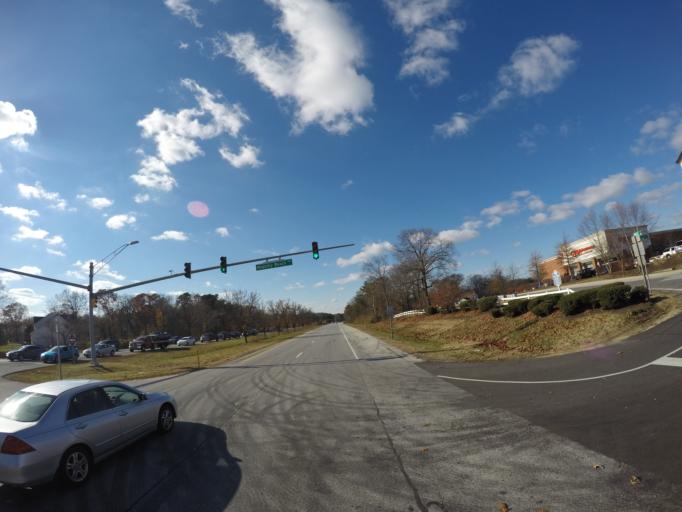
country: US
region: Maryland
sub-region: Anne Arundel County
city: Lake Shore
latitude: 39.1189
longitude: -76.5173
